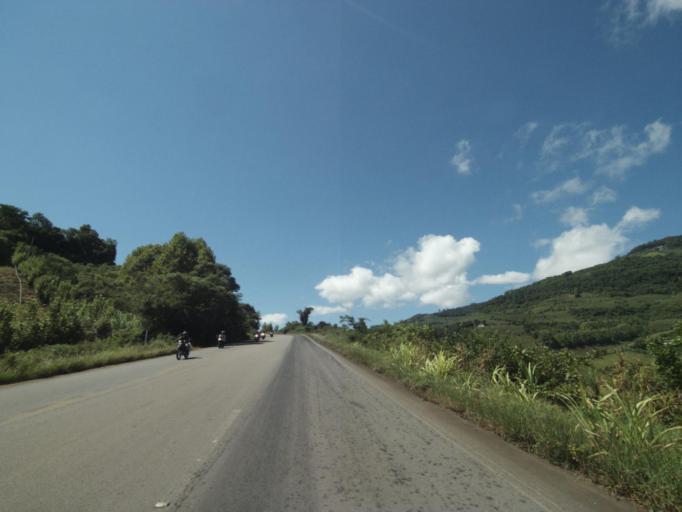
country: BR
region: Rio Grande do Sul
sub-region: Bento Goncalves
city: Bento Goncalves
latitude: -29.0988
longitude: -51.6269
